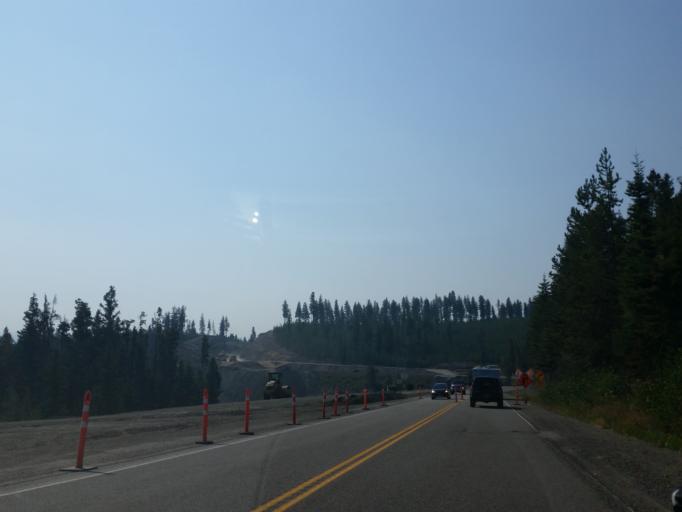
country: CA
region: British Columbia
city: Princeton
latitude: 49.2818
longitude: -120.5806
